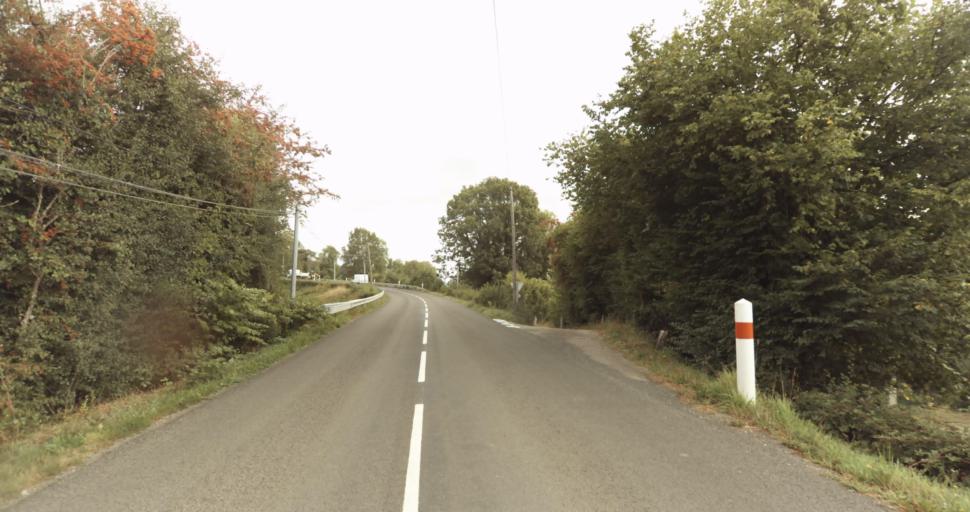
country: FR
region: Lower Normandy
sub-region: Departement de l'Orne
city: Vimoutiers
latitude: 48.9575
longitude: 0.2623
